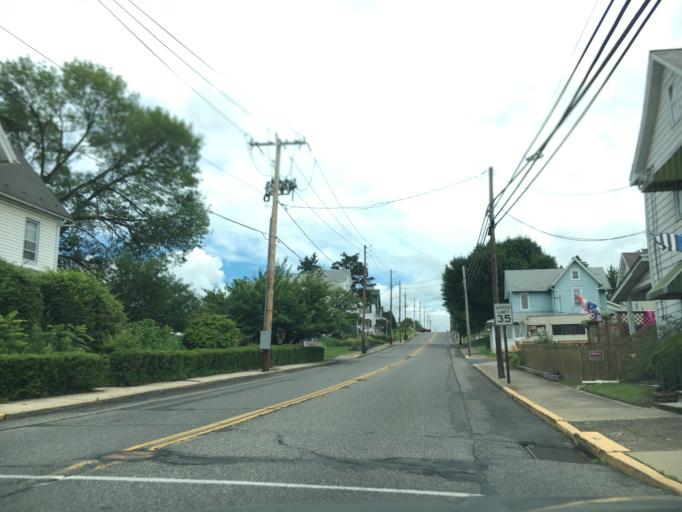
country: US
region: Pennsylvania
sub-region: Lehigh County
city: Cementon
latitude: 40.7010
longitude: -75.5044
